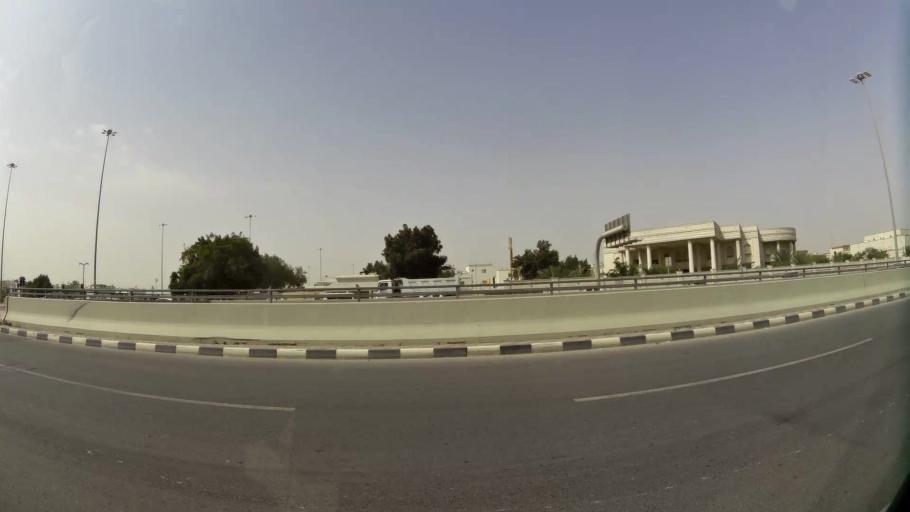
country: QA
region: Baladiyat ad Dawhah
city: Doha
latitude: 25.2763
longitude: 51.4890
